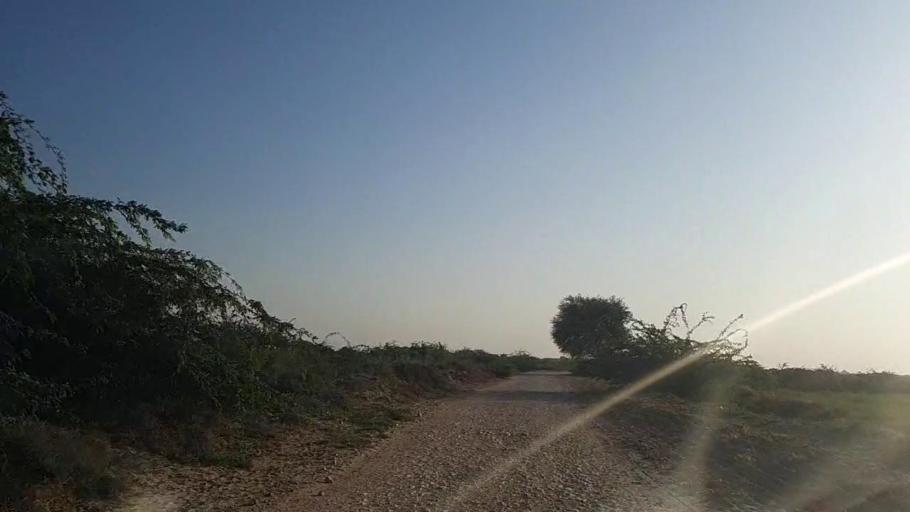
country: PK
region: Sindh
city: Jati
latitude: 24.4311
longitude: 68.1909
